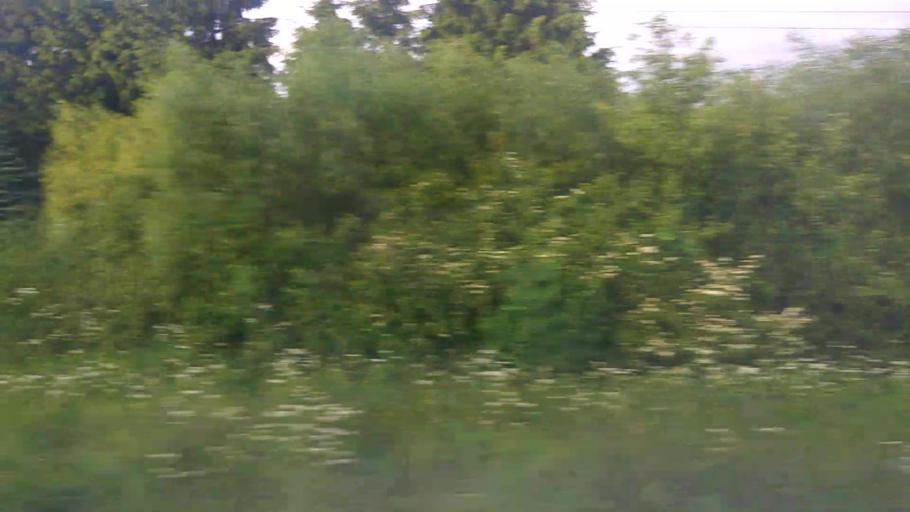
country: RU
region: Moskovskaya
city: Stupino
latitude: 54.8972
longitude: 38.0913
